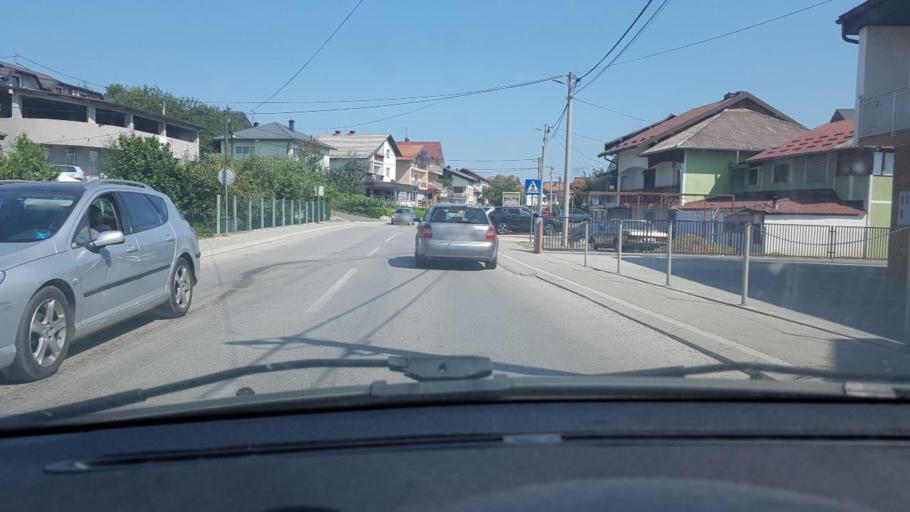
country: BA
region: Federation of Bosnia and Herzegovina
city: Velika Kladusa
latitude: 45.1885
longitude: 15.8113
